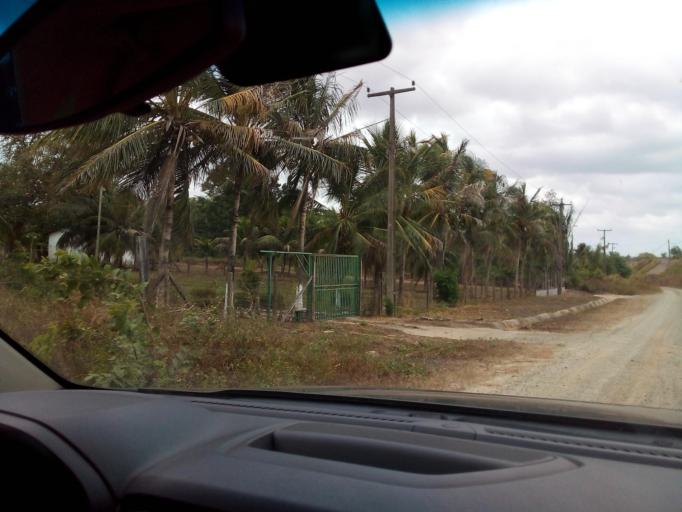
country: BR
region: Maranhao
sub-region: Sao Luis
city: Sao Luis
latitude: -2.6701
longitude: -44.2942
